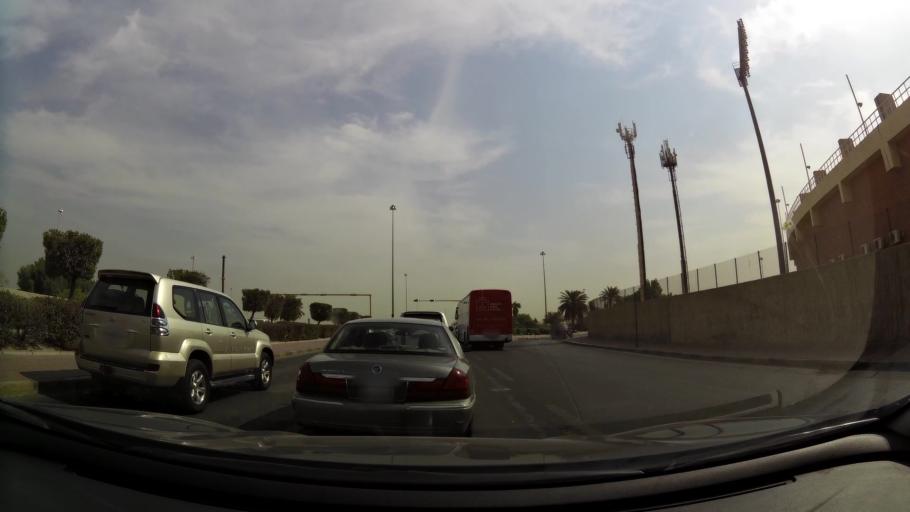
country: KW
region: Al Farwaniyah
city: Janub as Surrah
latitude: 29.2835
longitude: 47.9839
